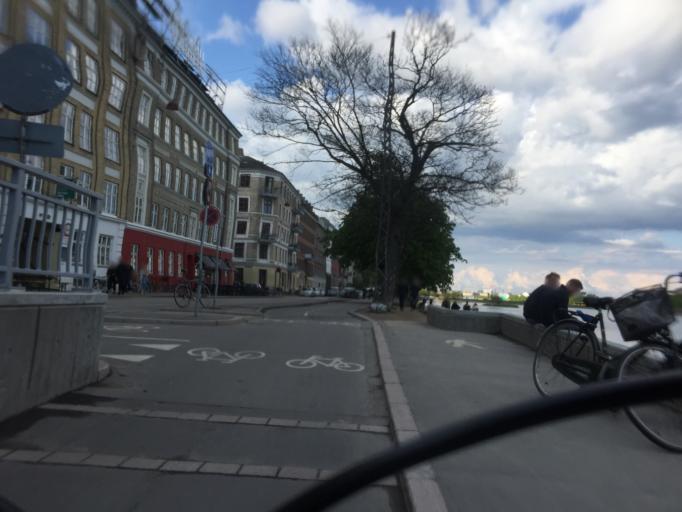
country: DK
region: Capital Region
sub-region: Kobenhavn
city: Copenhagen
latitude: 55.6878
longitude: 12.5631
